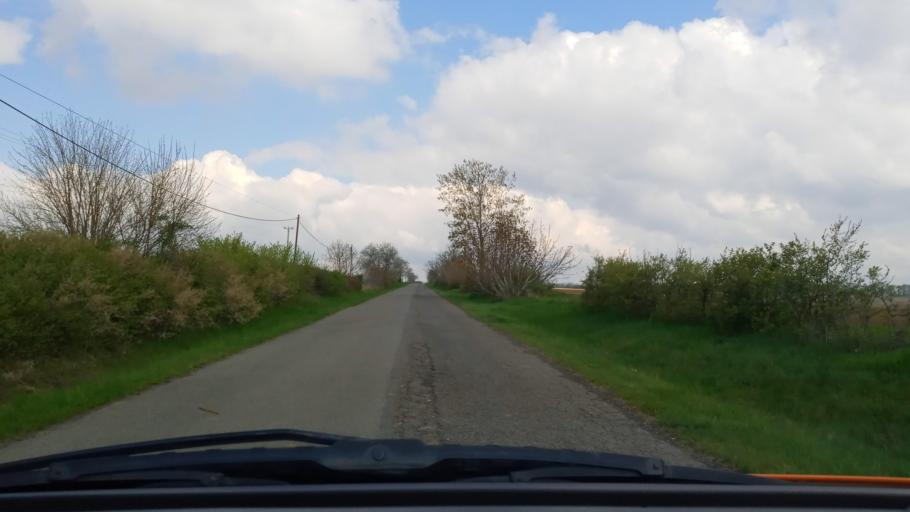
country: HU
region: Baranya
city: Pecsvarad
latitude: 46.0977
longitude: 18.4993
